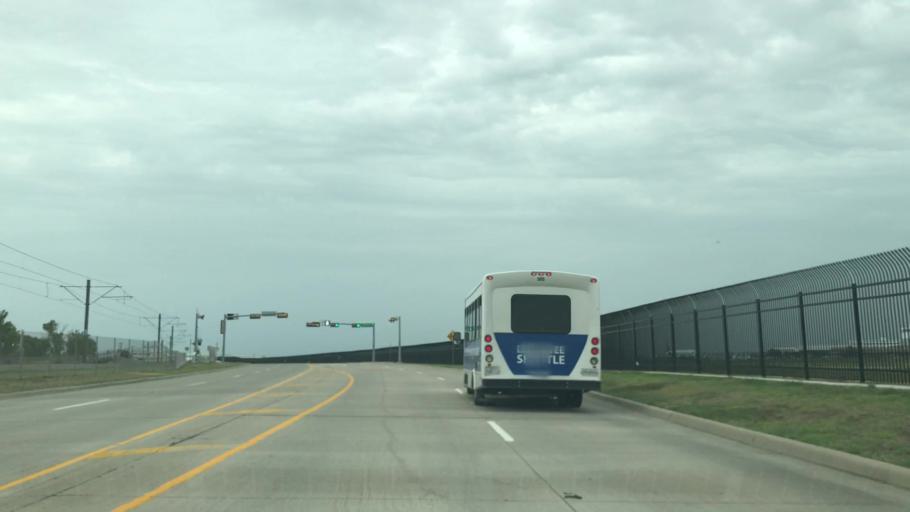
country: US
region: Texas
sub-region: Dallas County
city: University Park
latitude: 32.8365
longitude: -96.8489
